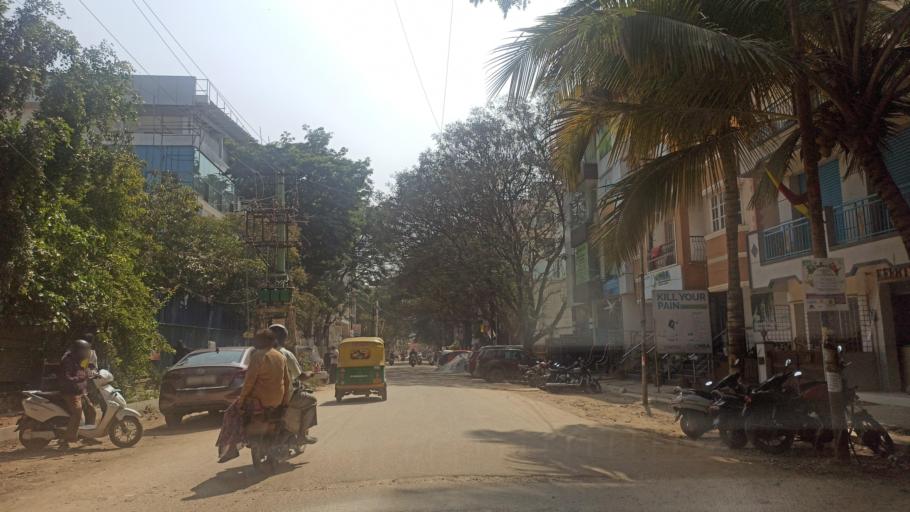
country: IN
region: Karnataka
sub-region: Bangalore Urban
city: Bangalore
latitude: 12.9625
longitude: 77.7134
